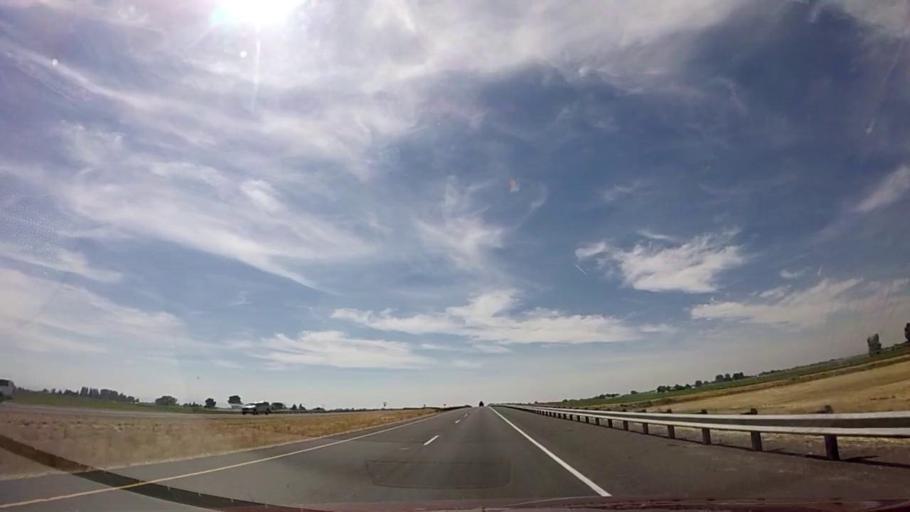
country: US
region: Idaho
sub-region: Minidoka County
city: Rupert
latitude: 42.5689
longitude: -113.6590
